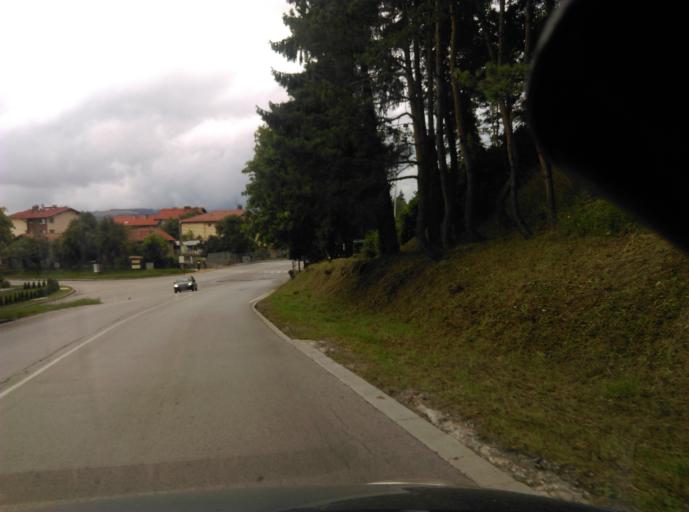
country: BG
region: Sofia-Capital
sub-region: Stolichna Obshtina
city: Sofia
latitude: 42.5911
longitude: 23.3642
